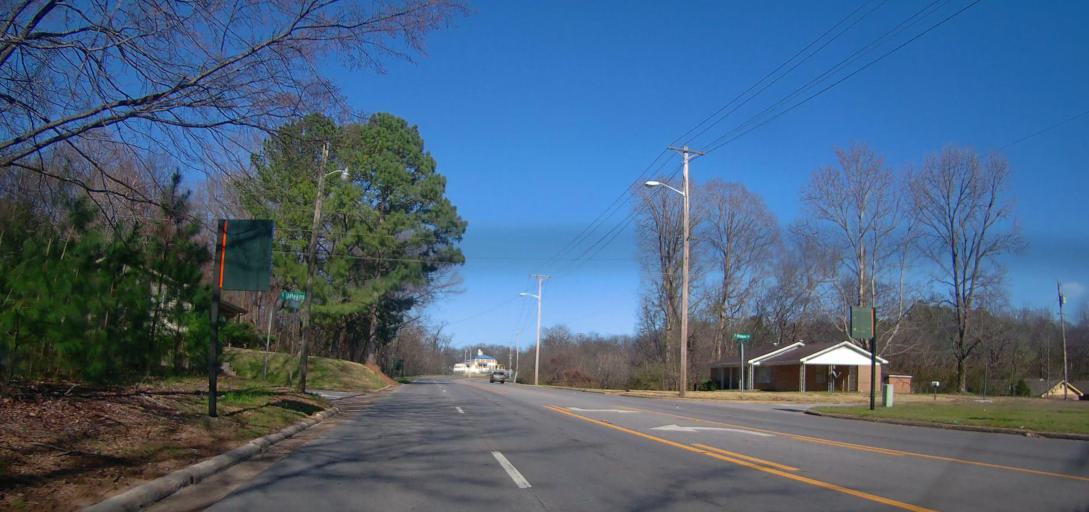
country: US
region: Alabama
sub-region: Lauderdale County
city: East Florence
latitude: 34.8115
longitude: -87.6322
